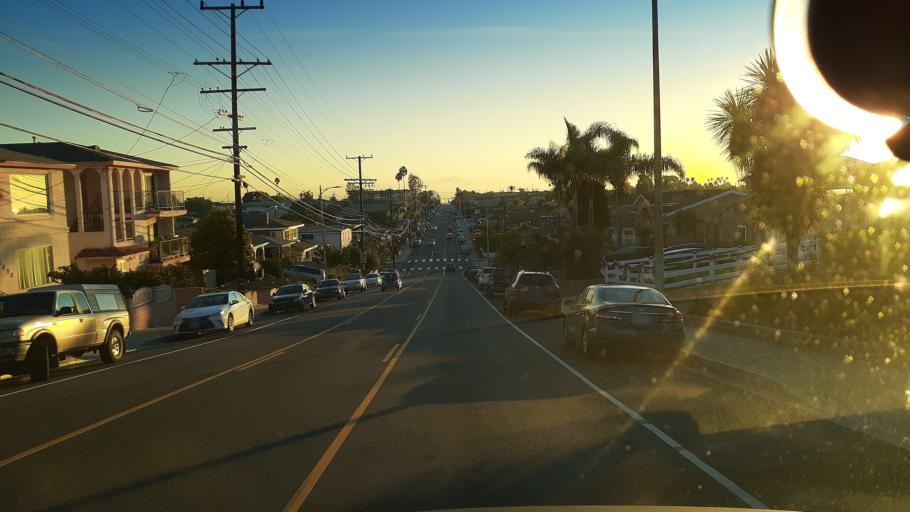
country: US
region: California
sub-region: Los Angeles County
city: San Pedro
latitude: 33.7216
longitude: -118.3051
